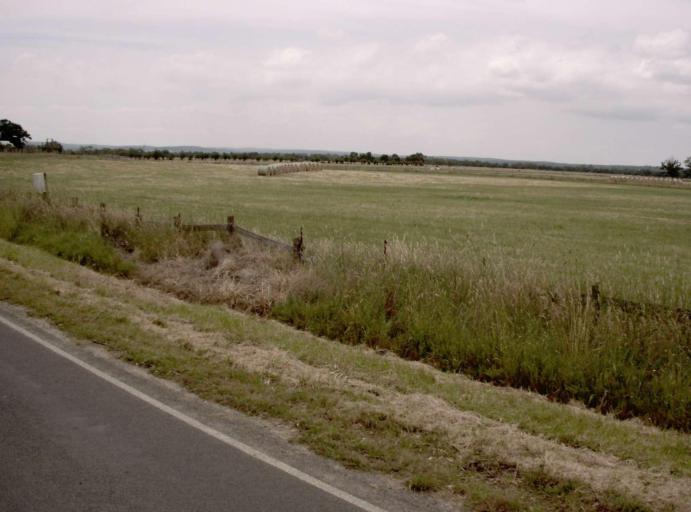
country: AU
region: Victoria
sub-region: Latrobe
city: Traralgon
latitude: -38.5226
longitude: 146.6604
